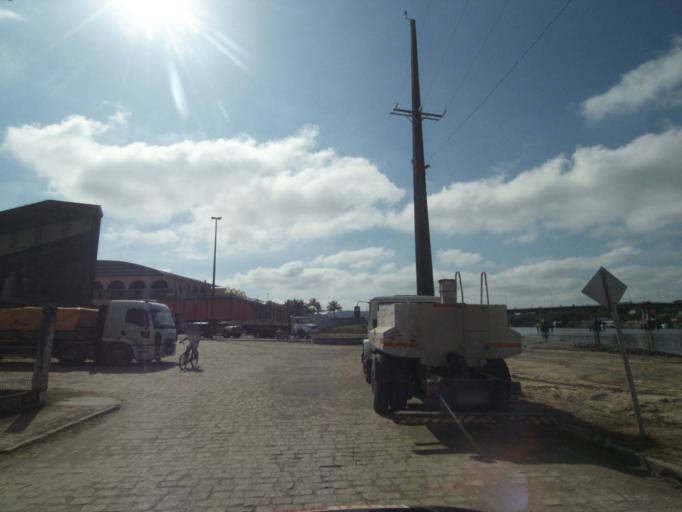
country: BR
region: Parana
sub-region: Paranagua
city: Paranagua
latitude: -25.5254
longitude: -48.5074
